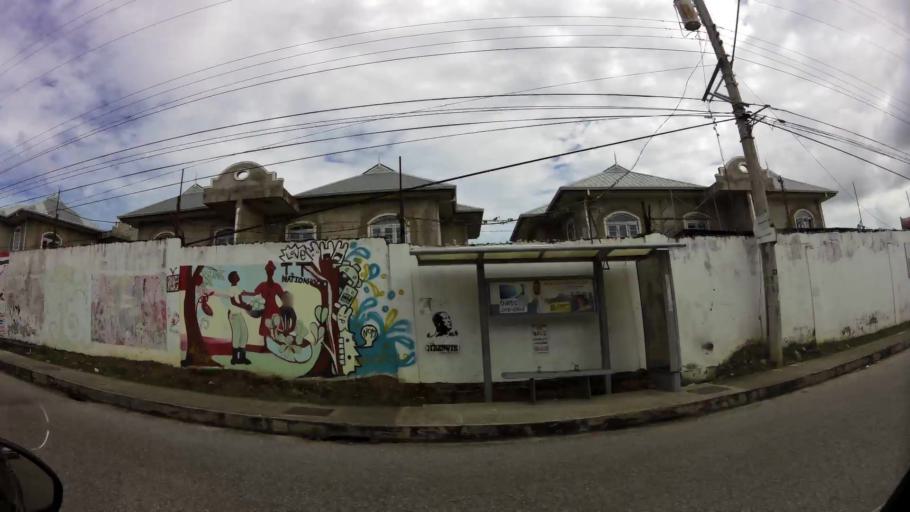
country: TT
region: City of Port of Spain
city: Port-of-Spain
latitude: 10.6768
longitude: -61.5298
